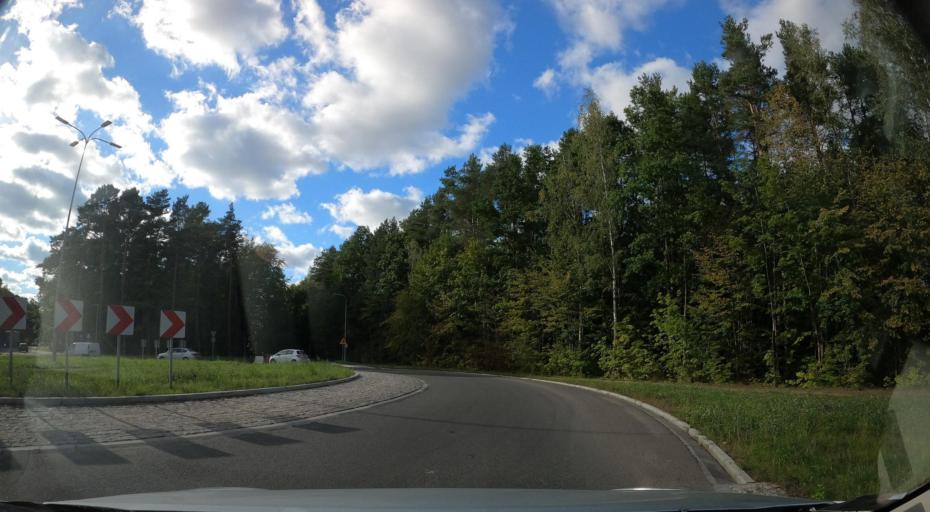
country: PL
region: Pomeranian Voivodeship
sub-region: Powiat wejherowski
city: Luzino
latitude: 54.5689
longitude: 18.0511
